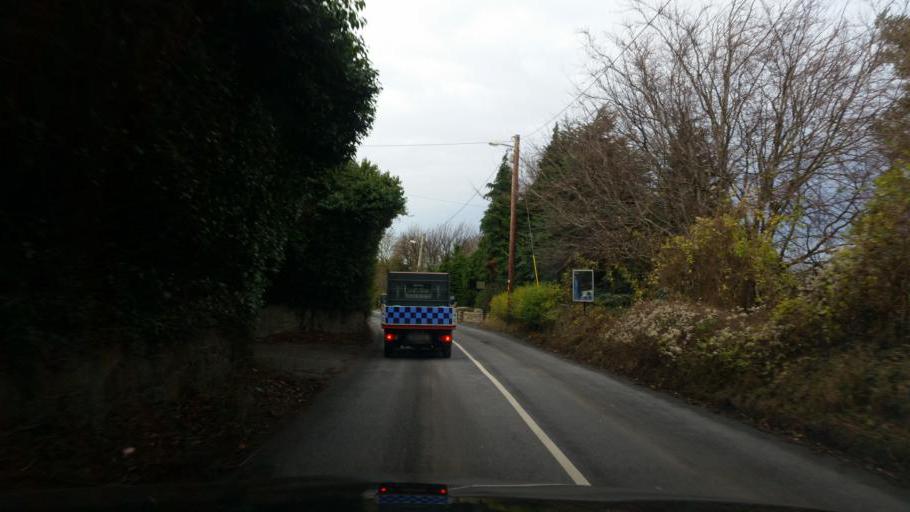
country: IE
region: Leinster
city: Balally
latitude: 53.2663
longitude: -6.2442
